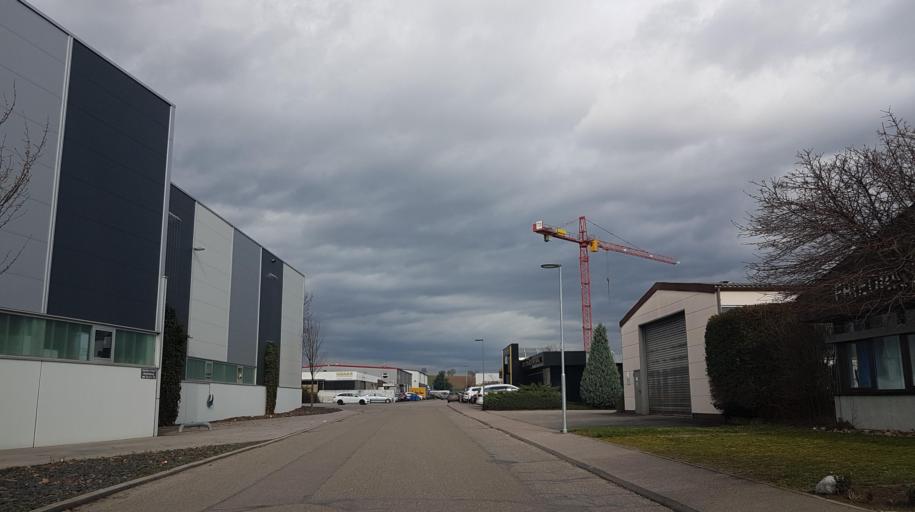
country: DE
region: Baden-Wuerttemberg
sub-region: Regierungsbezirk Stuttgart
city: Untereisesheim
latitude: 49.2346
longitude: 9.2189
